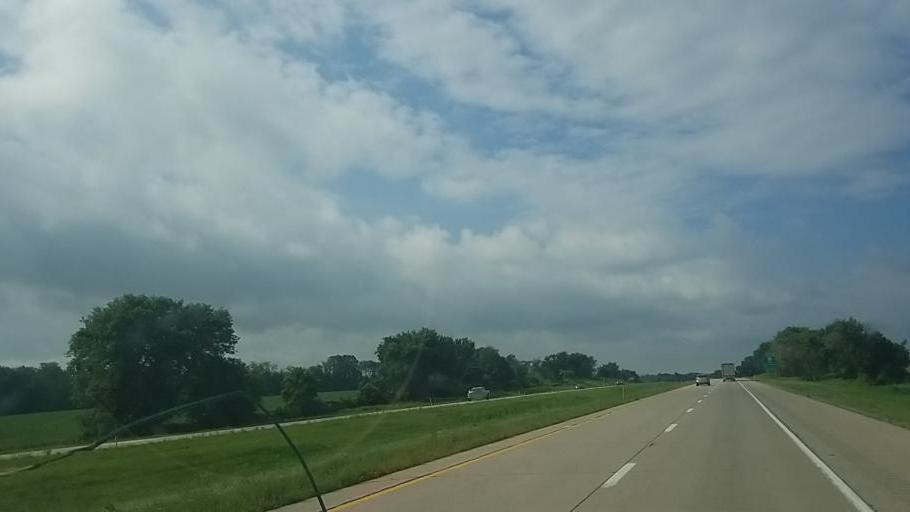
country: US
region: Pennsylvania
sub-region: Centre County
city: Bellefonte
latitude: 40.9308
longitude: -77.7375
